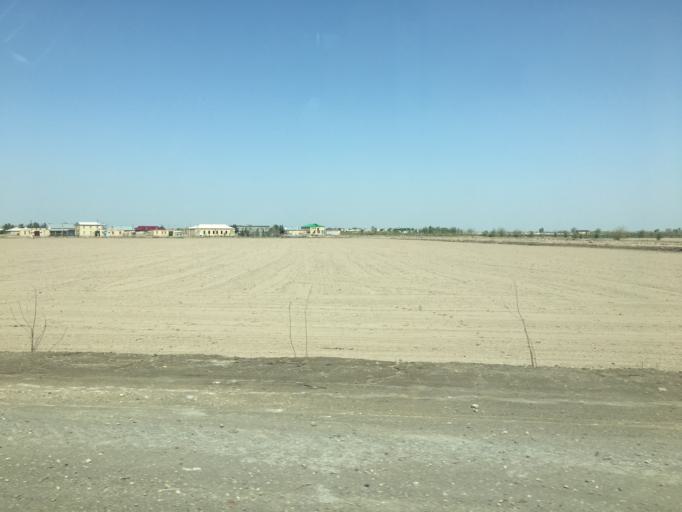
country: TM
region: Lebap
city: Turkmenabat
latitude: 39.0078
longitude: 63.6079
